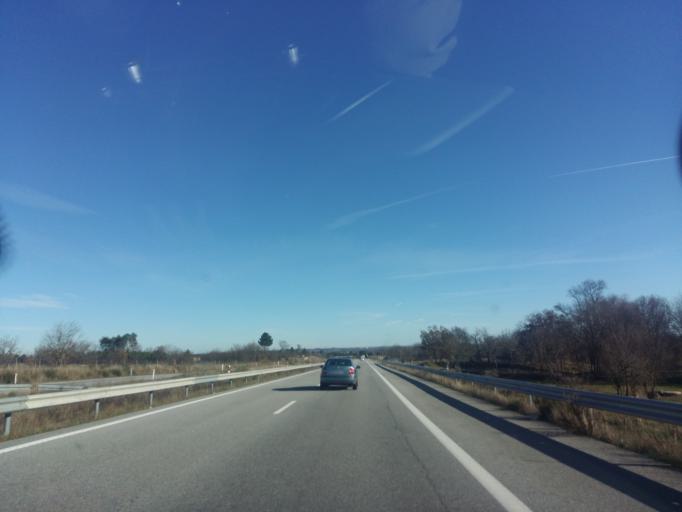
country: PT
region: Guarda
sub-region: Guarda
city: Sequeira
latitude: 40.6005
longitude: -7.1247
